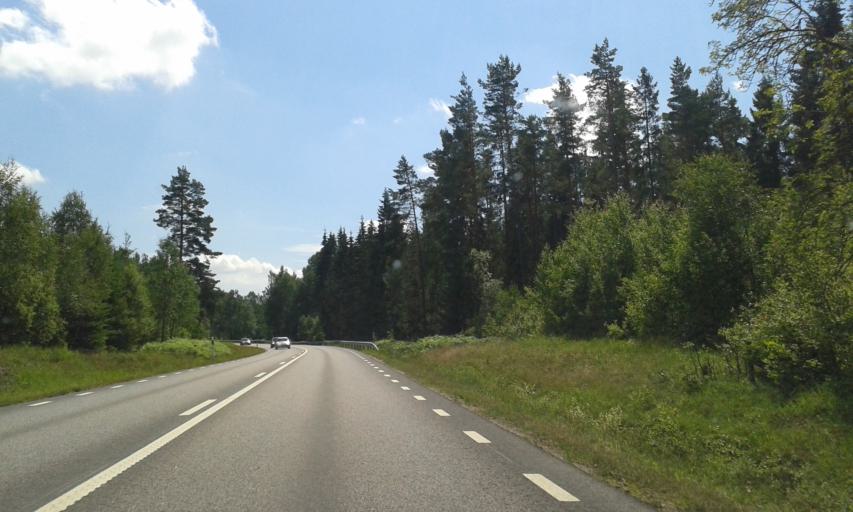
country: SE
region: Kronoberg
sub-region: Vaxjo Kommun
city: Ingelstad
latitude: 56.7863
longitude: 14.8990
